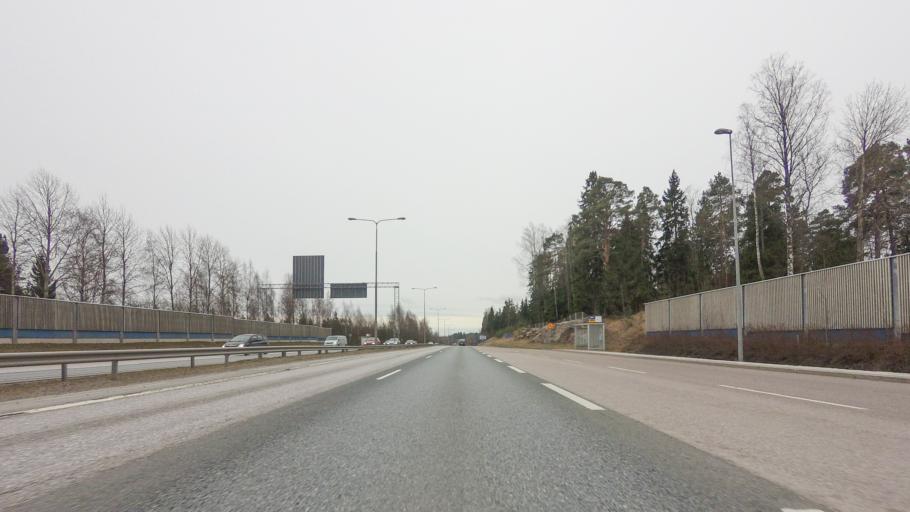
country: FI
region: Uusimaa
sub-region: Helsinki
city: Teekkarikylae
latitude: 60.2842
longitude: 24.8646
